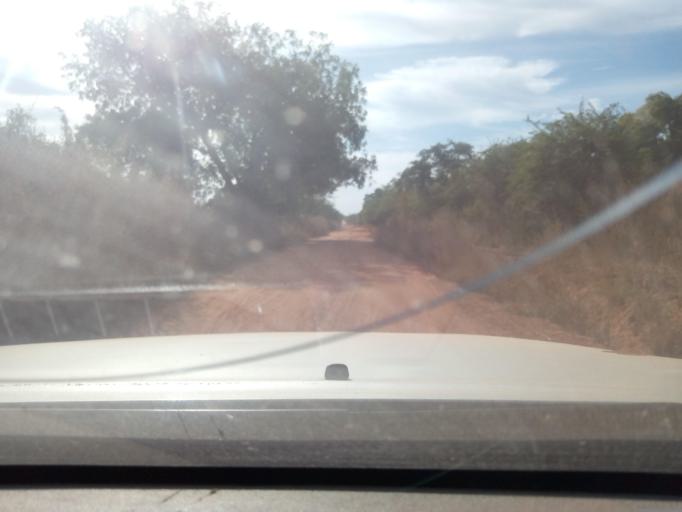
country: ML
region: Sikasso
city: Sikasso
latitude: 11.9236
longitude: -6.0681
